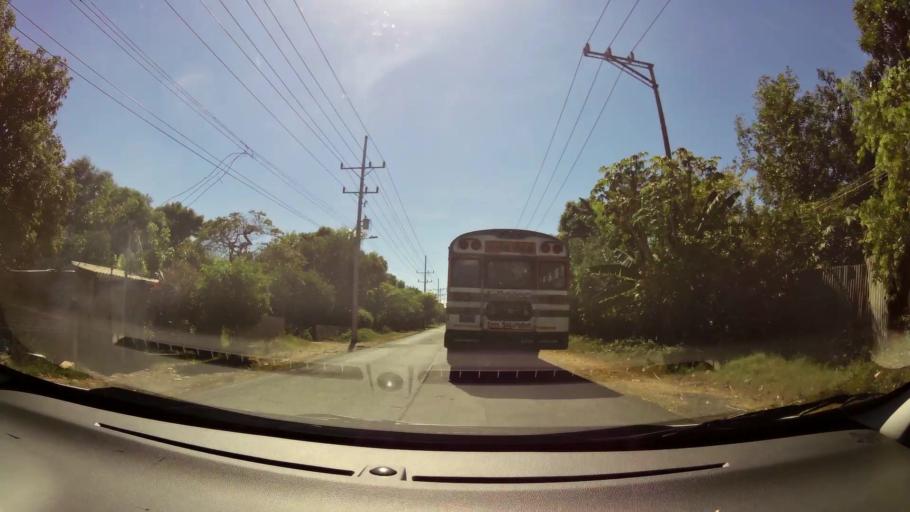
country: SV
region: La Libertad
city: San Juan Opico
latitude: 13.8466
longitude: -89.3618
